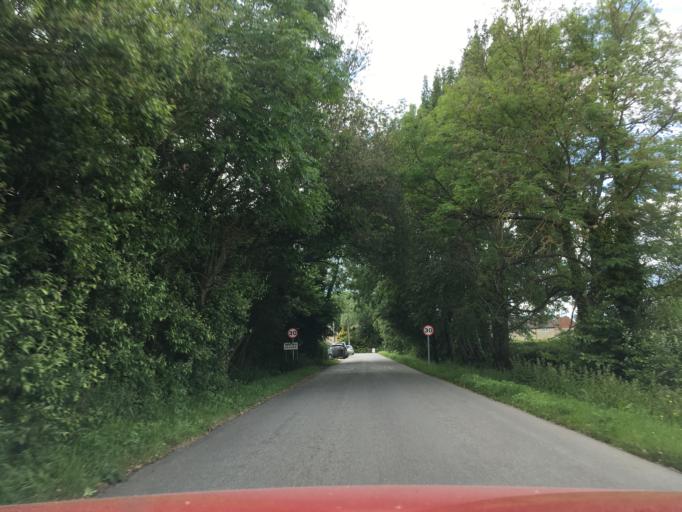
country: GB
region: England
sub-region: Wiltshire
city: Minety
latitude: 51.6422
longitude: -1.9283
